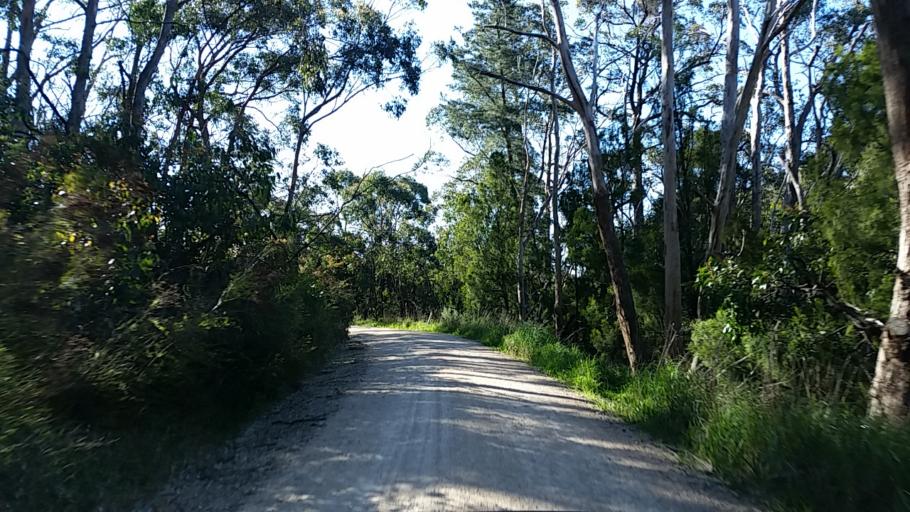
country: AU
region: South Australia
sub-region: Adelaide Hills
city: Lobethal
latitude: -34.8881
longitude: 138.8512
